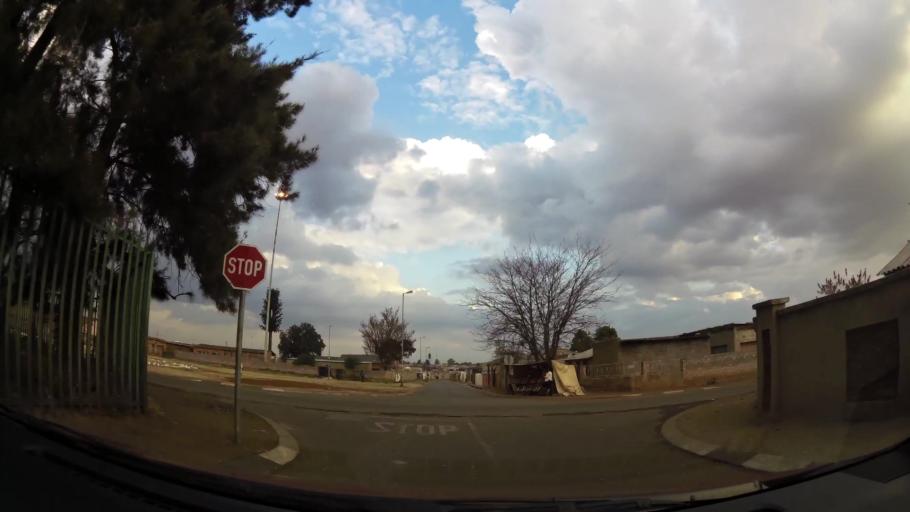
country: ZA
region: Gauteng
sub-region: City of Johannesburg Metropolitan Municipality
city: Soweto
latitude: -26.2466
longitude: 27.8248
